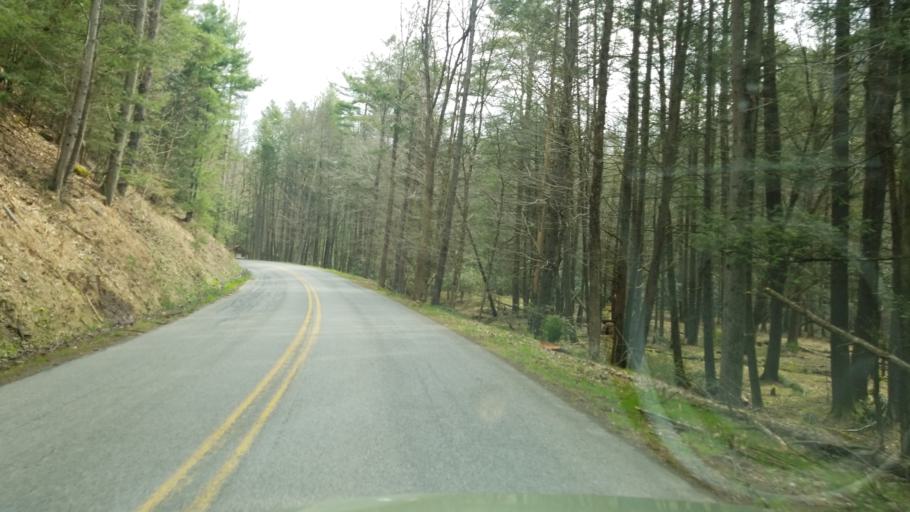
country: US
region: Pennsylvania
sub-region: Cameron County
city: Emporium
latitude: 41.2981
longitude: -78.1074
